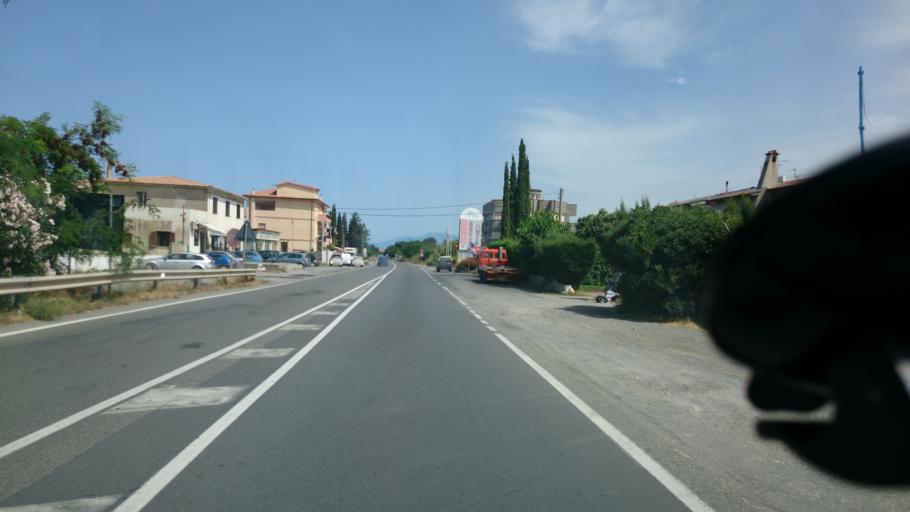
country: IT
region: Calabria
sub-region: Provincia di Cosenza
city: Diamante
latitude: 39.6852
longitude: 15.8196
